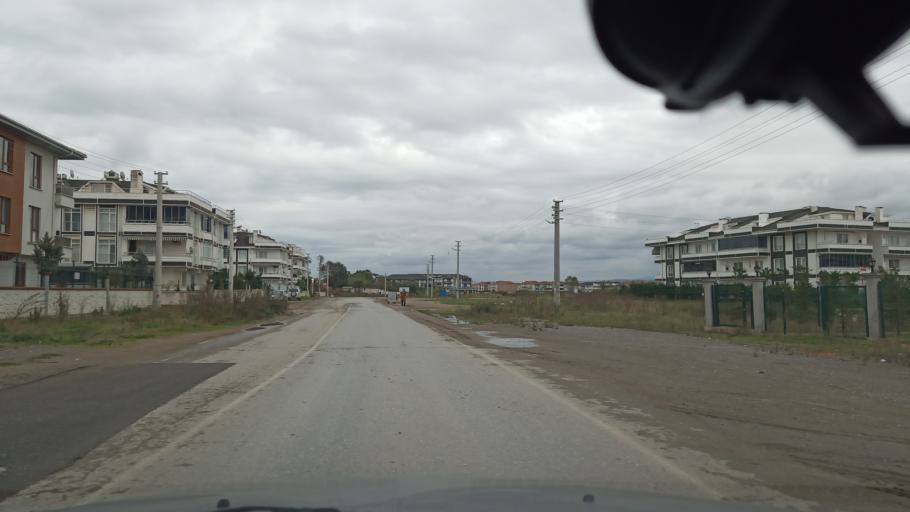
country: TR
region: Sakarya
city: Karasu
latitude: 41.1141
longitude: 30.6732
